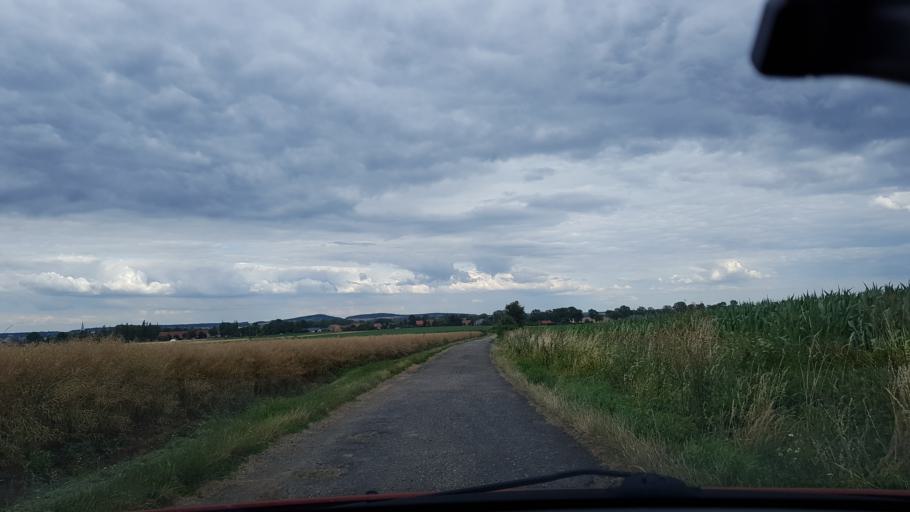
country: PL
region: Lower Silesian Voivodeship
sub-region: Powiat zabkowicki
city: Zabkowice Slaskie
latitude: 50.5709
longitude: 16.7742
